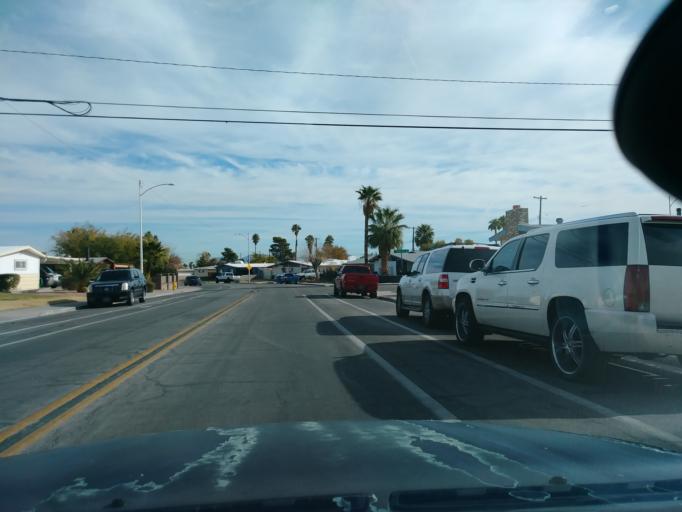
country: US
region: Nevada
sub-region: Clark County
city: Spring Valley
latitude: 36.1706
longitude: -115.2294
